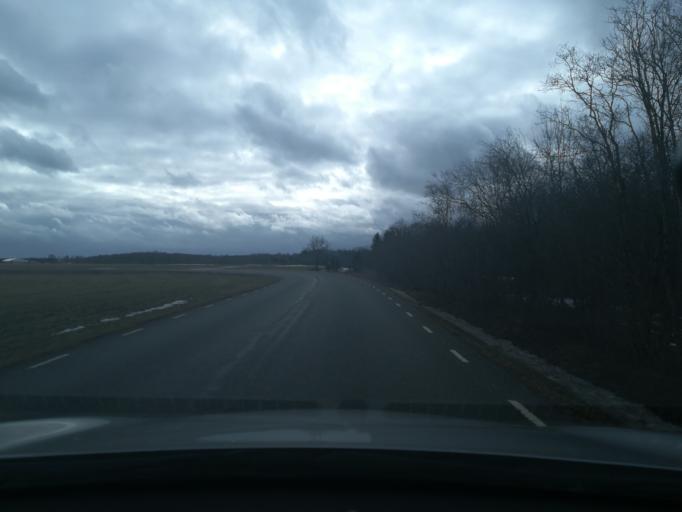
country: EE
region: Harju
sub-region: Saue linn
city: Saue
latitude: 59.3490
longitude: 24.5387
